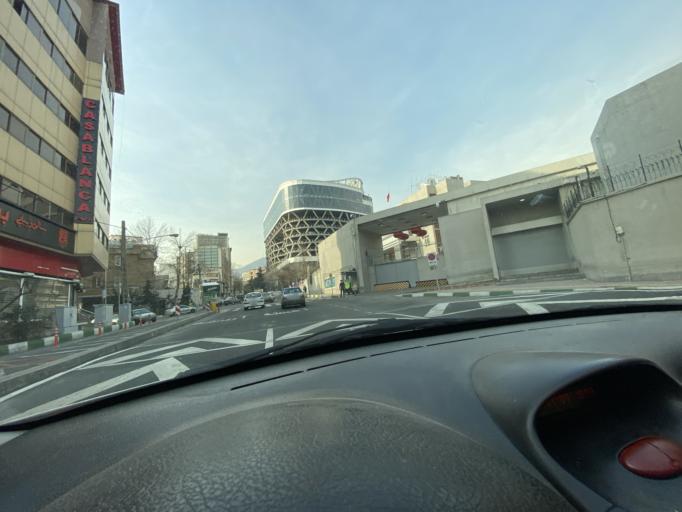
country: IR
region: Tehran
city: Tajrish
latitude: 35.8039
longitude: 51.4777
